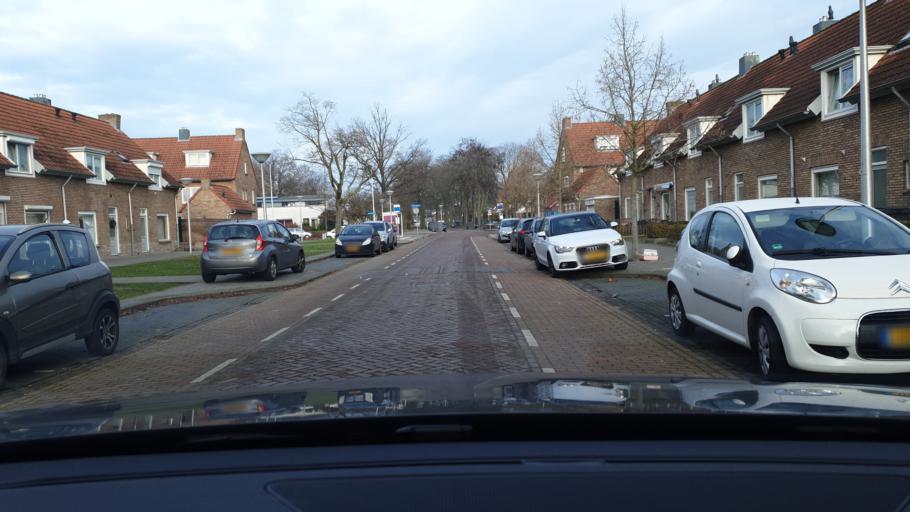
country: NL
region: North Brabant
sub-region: Gemeente Eindhoven
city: De Doornakkers
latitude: 51.4385
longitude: 5.5134
